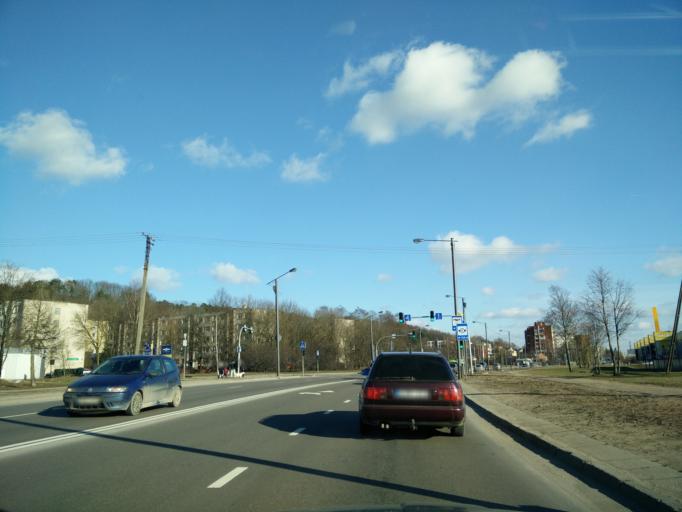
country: LT
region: Kauno apskritis
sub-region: Kauno rajonas
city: Akademija (Kaunas)
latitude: 54.9202
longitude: 23.8256
